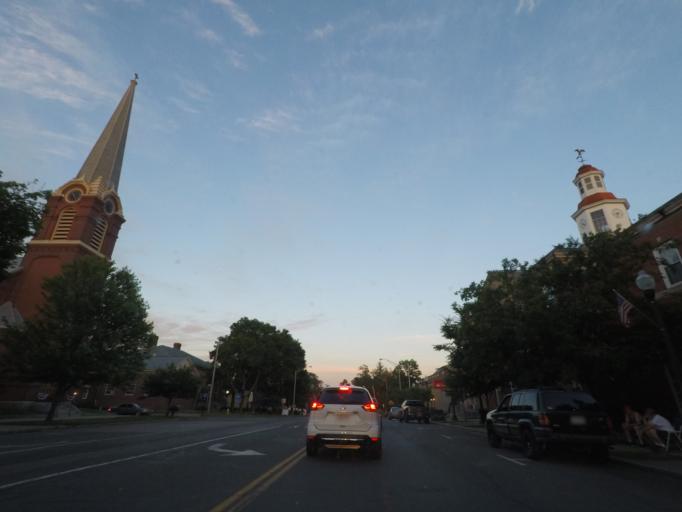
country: US
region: Massachusetts
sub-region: Worcester County
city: Southbridge
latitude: 42.0748
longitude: -72.0334
